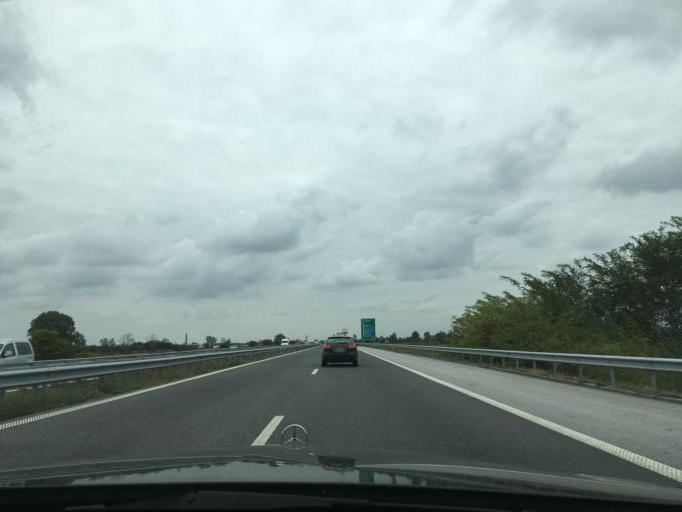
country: BG
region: Pazardzhik
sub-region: Obshtina Pazardzhik
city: Pazardzhik
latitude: 42.2682
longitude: 24.2995
